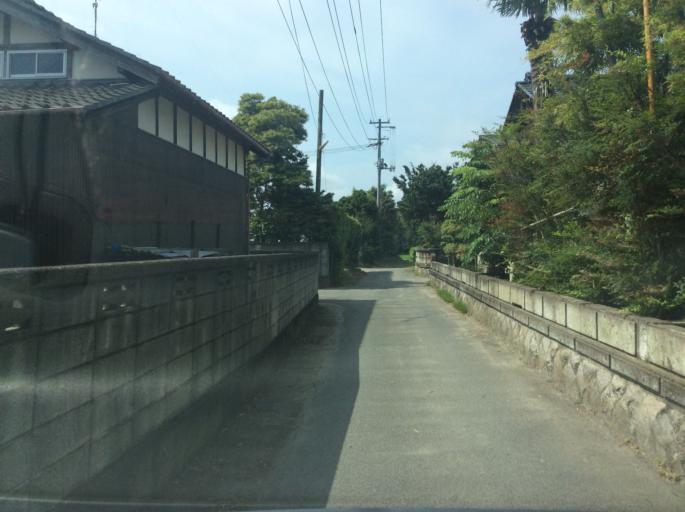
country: JP
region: Fukushima
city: Iwaki
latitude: 37.0663
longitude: 140.9615
